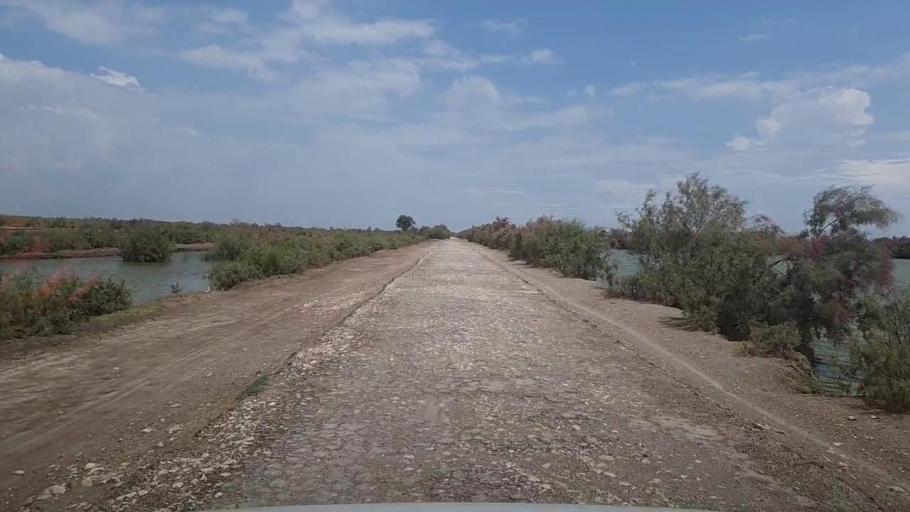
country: PK
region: Sindh
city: Kandhkot
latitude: 28.3419
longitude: 69.2238
